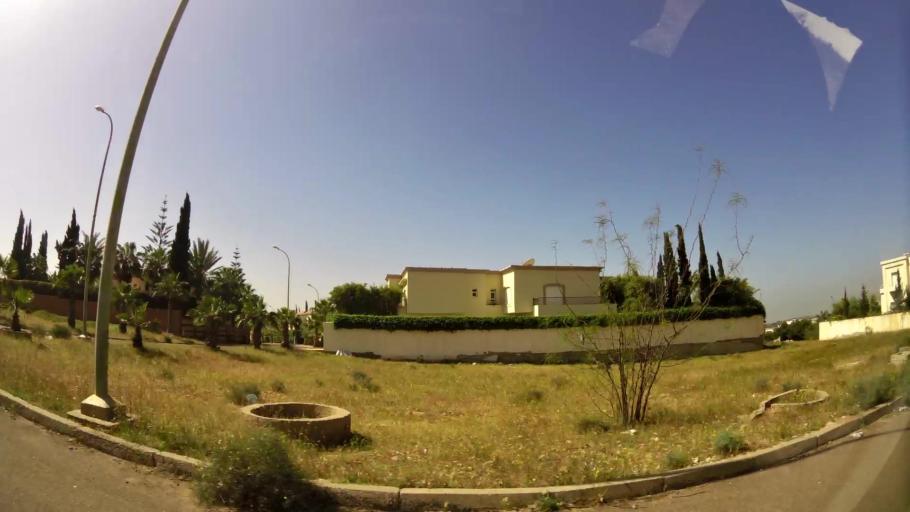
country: MA
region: Souss-Massa-Draa
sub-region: Agadir-Ida-ou-Tnan
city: Agadir
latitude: 30.4420
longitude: -9.5829
